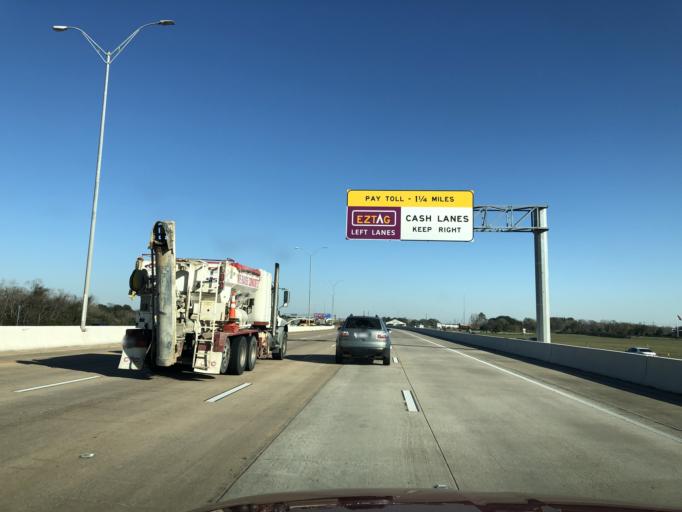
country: US
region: Texas
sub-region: Fort Bend County
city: Fresno
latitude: 29.5964
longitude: -95.4365
